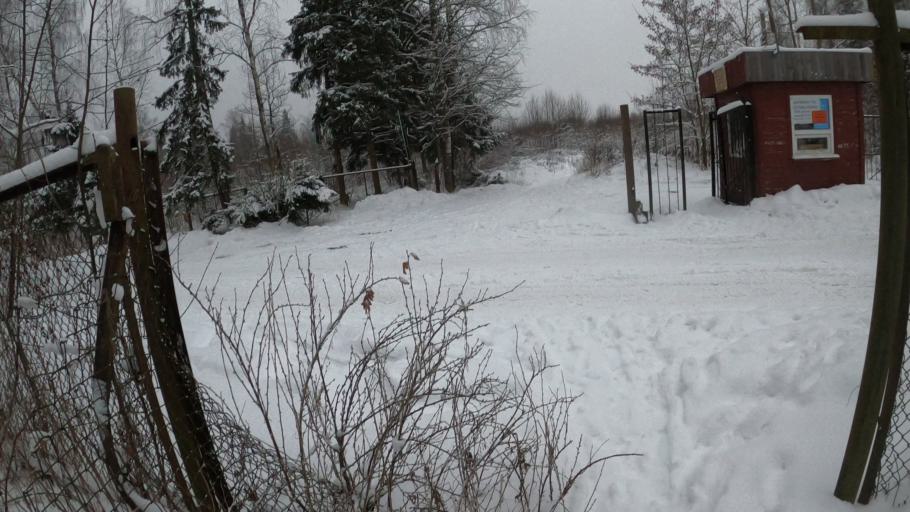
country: RU
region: Moskovskaya
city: Firsanovka
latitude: 55.9123
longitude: 37.2041
